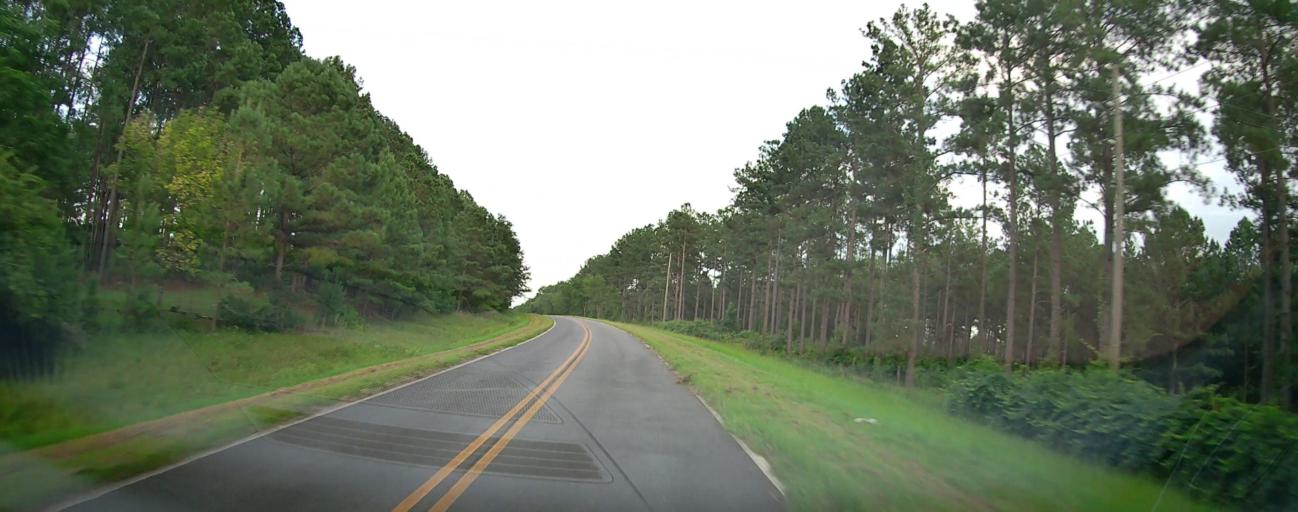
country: US
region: Georgia
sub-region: Crawford County
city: Roberta
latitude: 32.6579
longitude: -84.0595
